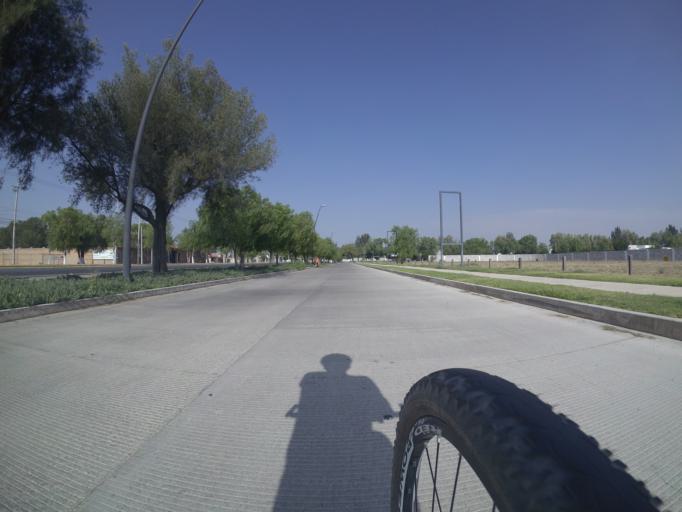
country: MX
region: Aguascalientes
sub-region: Jesus Maria
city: El Llano
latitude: 21.9493
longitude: -102.3154
